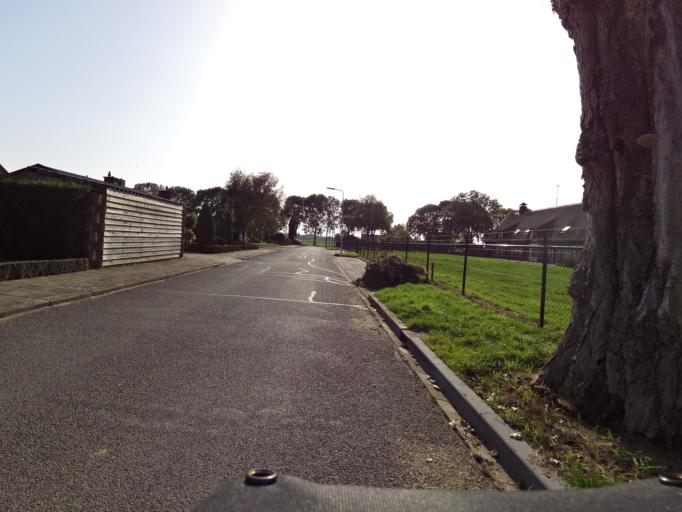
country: NL
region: Gelderland
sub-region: Gemeente Duiven
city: Duiven
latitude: 51.8917
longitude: 5.9930
